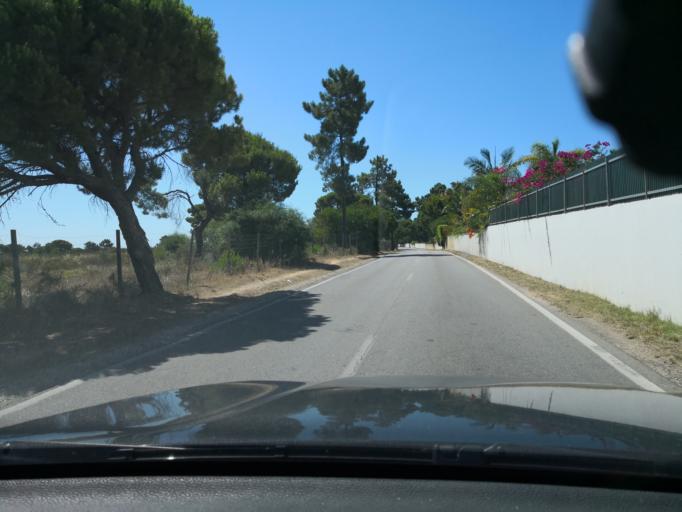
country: PT
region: Faro
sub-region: Loule
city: Vilamoura
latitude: 37.0843
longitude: -8.1006
